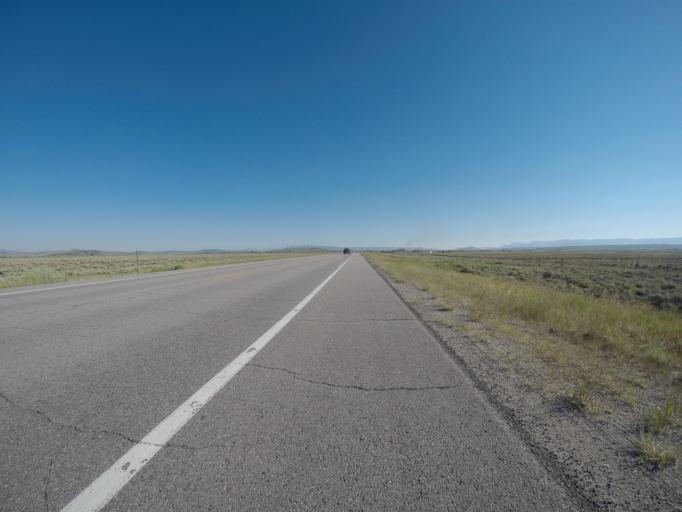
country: US
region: Wyoming
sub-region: Sublette County
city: Pinedale
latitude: 42.9630
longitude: -110.0883
